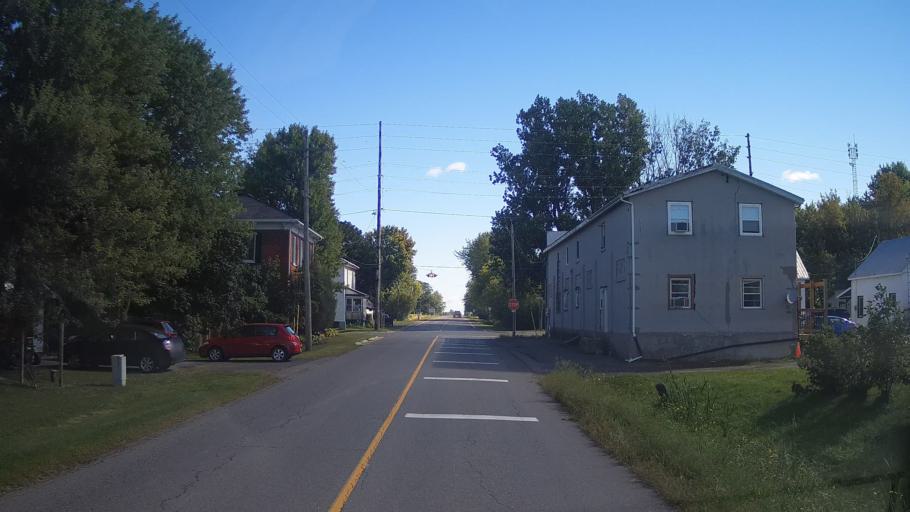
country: CA
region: Ontario
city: Prescott
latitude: 44.9234
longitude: -75.3482
